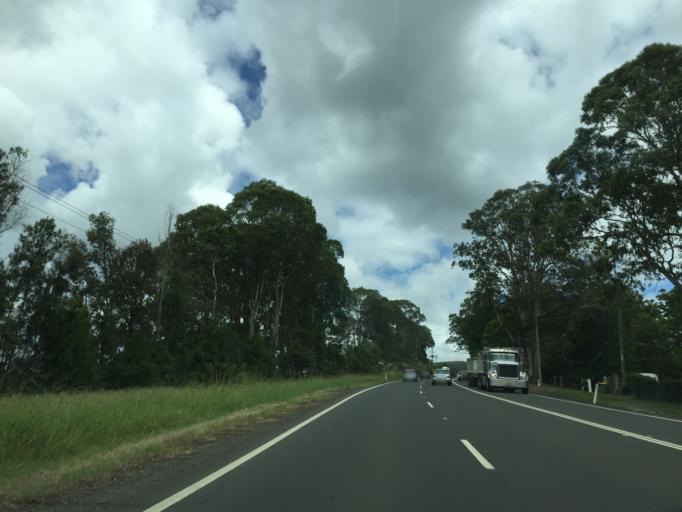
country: AU
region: New South Wales
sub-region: Hawkesbury
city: Richmond
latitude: -33.5472
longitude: 150.6585
